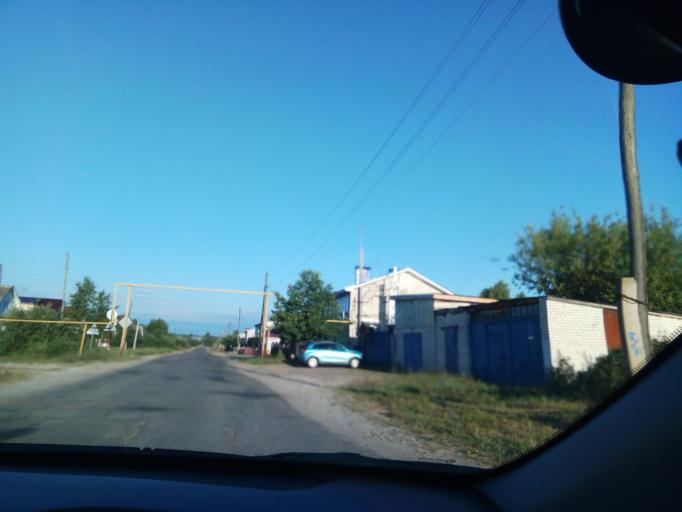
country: RU
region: Nizjnij Novgorod
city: Voznesenskoye
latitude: 54.8889
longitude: 42.7888
